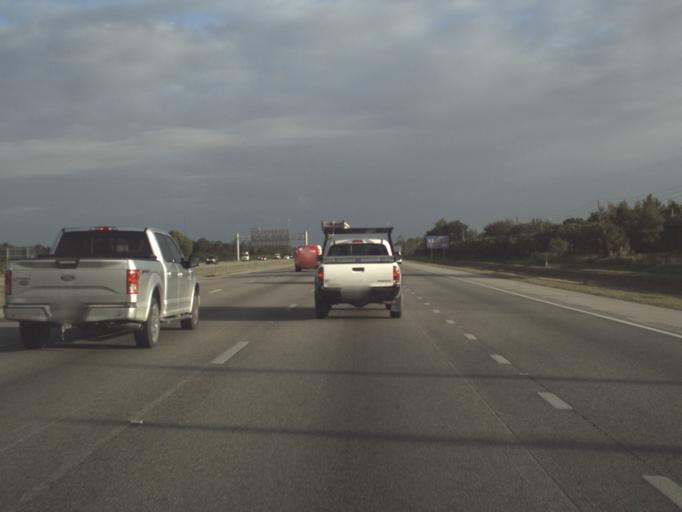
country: US
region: Florida
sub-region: Lee County
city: Gateway
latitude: 26.5347
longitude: -81.7947
